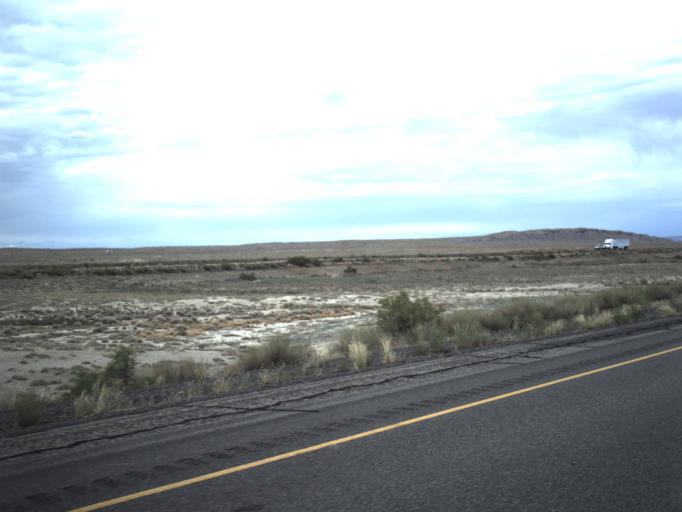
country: US
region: Utah
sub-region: Grand County
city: Moab
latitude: 38.9392
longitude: -109.5060
